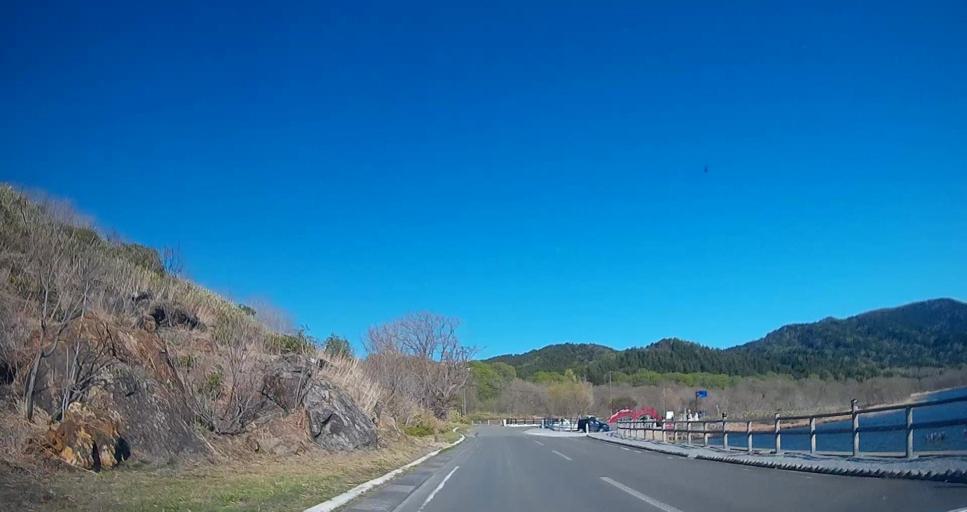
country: JP
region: Aomori
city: Mutsu
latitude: 41.3265
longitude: 141.0953
